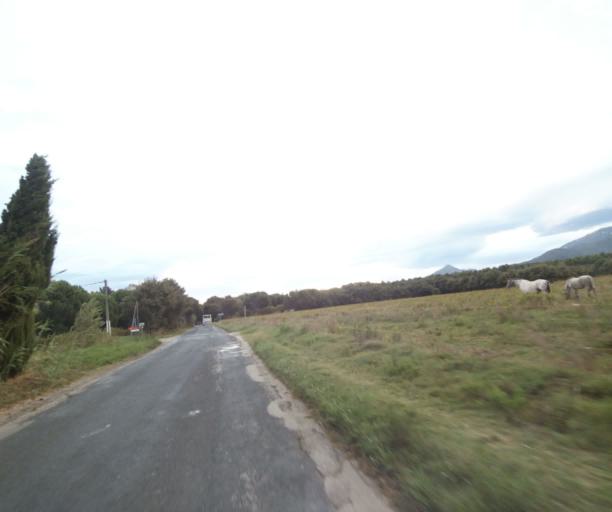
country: FR
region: Languedoc-Roussillon
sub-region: Departement des Pyrenees-Orientales
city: Argelers
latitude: 42.5628
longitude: 3.0127
